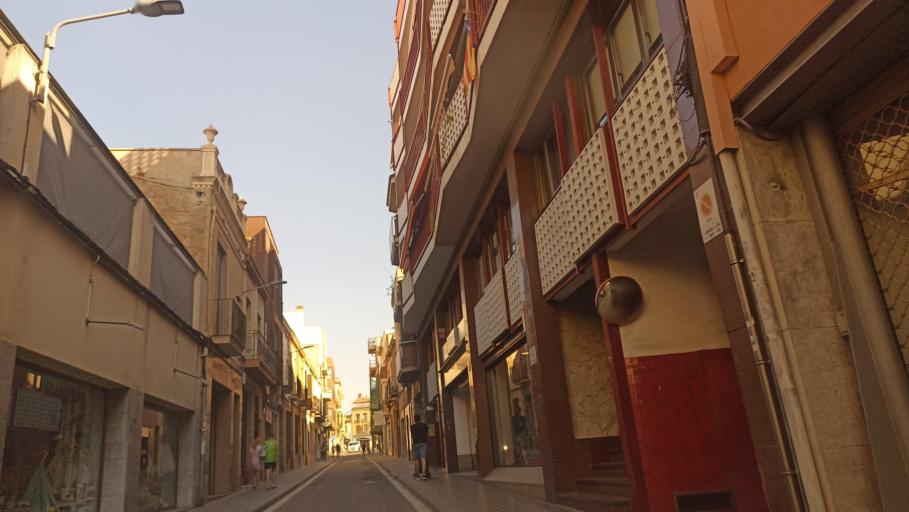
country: ES
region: Catalonia
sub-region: Provincia de Barcelona
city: Mataro
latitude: 41.5372
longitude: 2.4427
